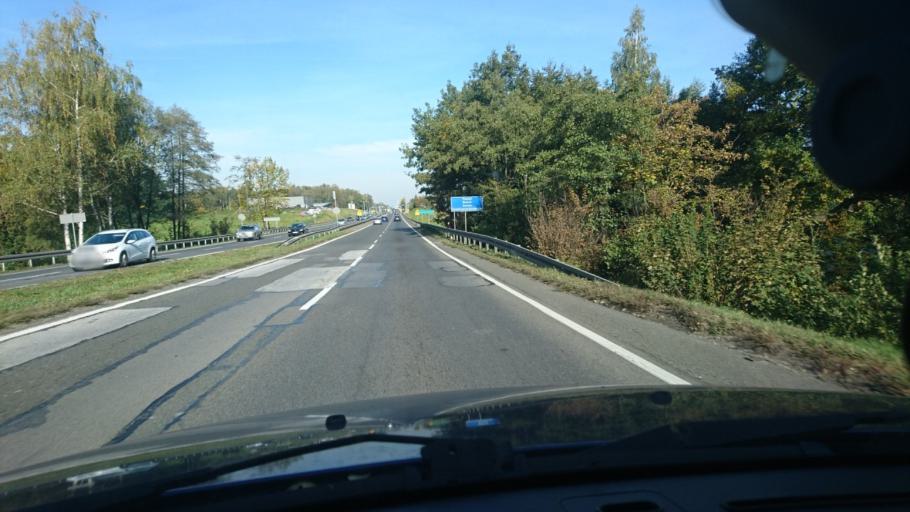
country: PL
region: Silesian Voivodeship
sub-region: Powiat bielski
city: Mazancowice
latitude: 49.8649
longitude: 19.0130
